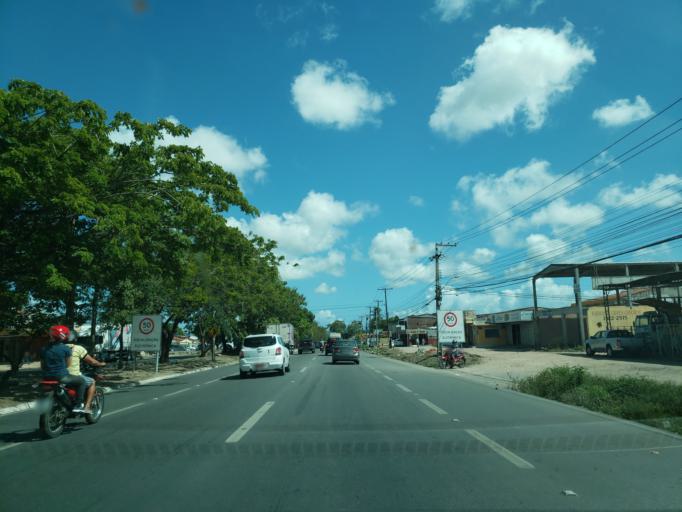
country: BR
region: Alagoas
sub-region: Satuba
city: Satuba
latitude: -9.5438
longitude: -35.7895
